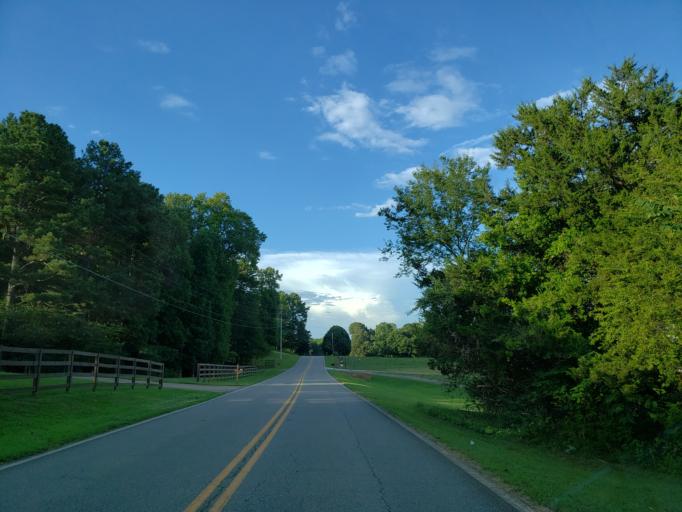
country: US
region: Georgia
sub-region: Cherokee County
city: Canton
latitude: 34.3145
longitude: -84.5316
